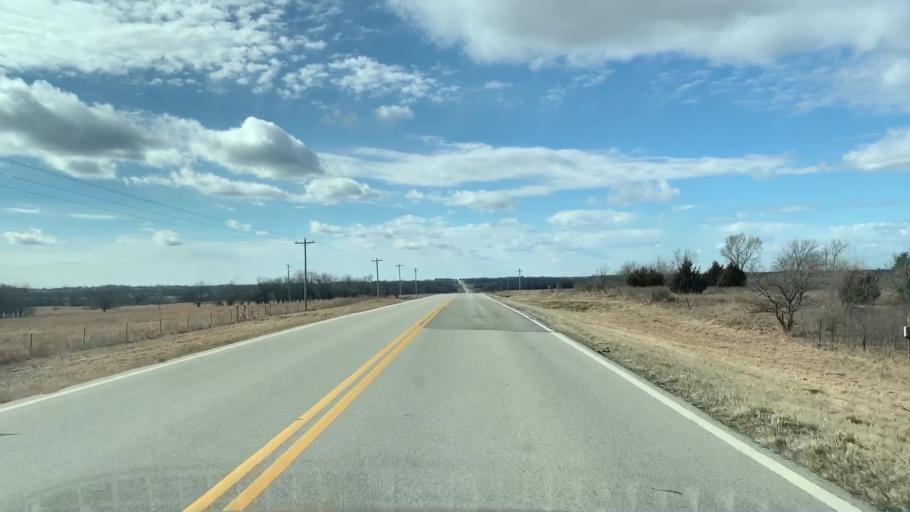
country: US
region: Kansas
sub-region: Neosho County
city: Erie
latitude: 37.5291
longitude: -95.3859
